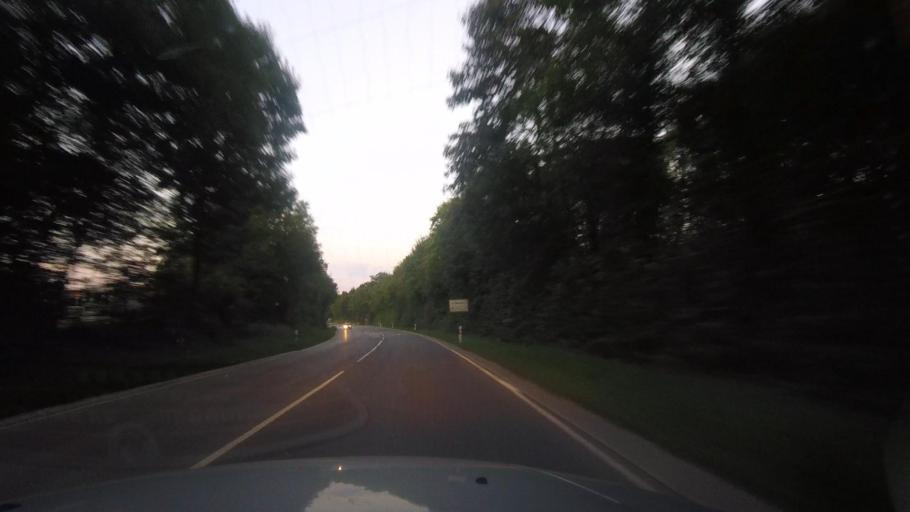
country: DE
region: Baden-Wuerttemberg
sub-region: Regierungsbezirk Stuttgart
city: Freiberg am Neckar
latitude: 48.9399
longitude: 9.2104
